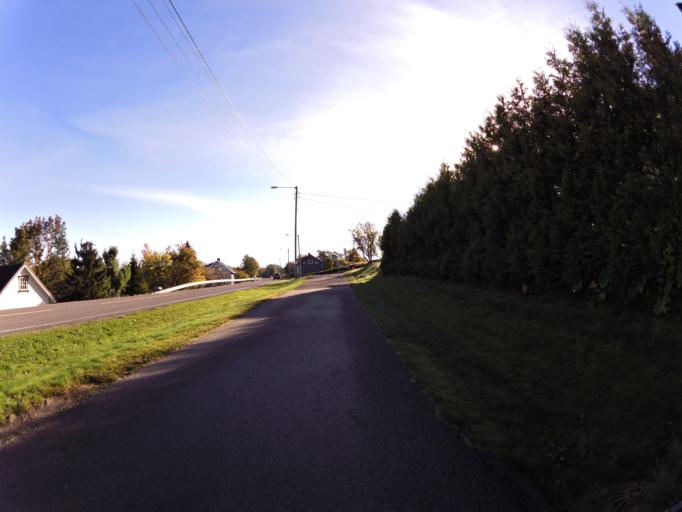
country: NO
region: Ostfold
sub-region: Fredrikstad
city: Fredrikstad
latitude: 59.2907
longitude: 10.9995
